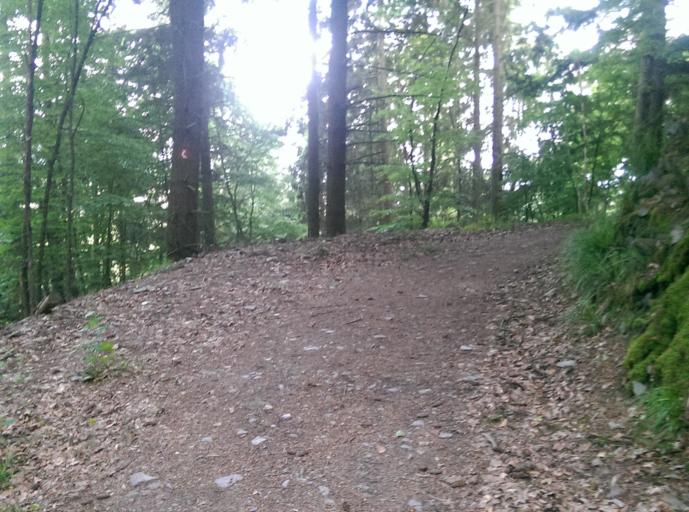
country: DE
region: Rheinland-Pfalz
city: Melsbach
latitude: 50.4906
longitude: 7.4607
